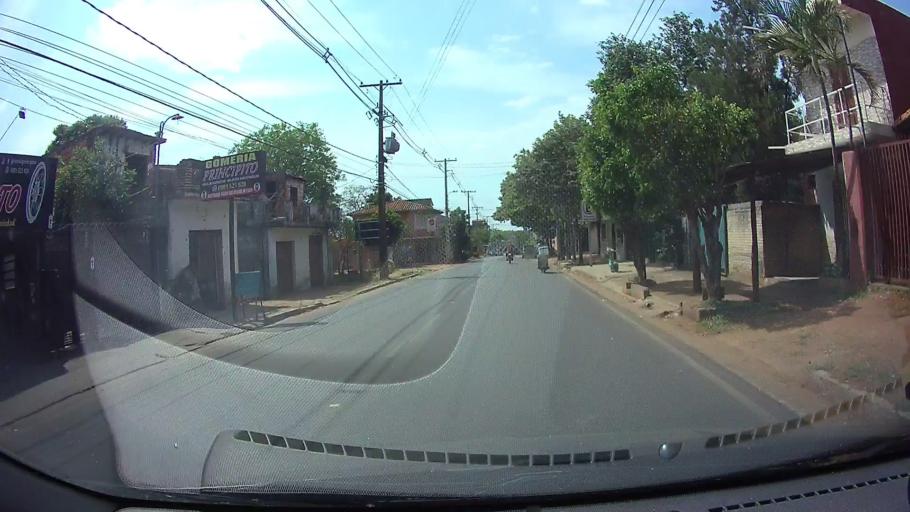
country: PY
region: Central
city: San Lorenzo
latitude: -25.3366
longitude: -57.4916
